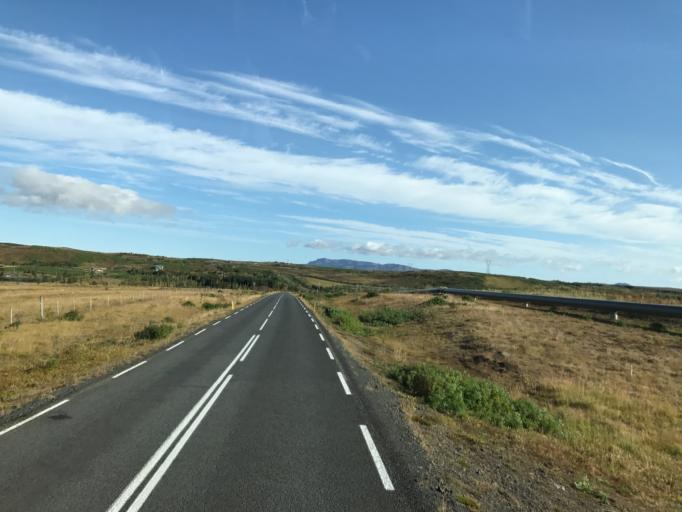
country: IS
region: Capital Region
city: Mosfellsbaer
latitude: 64.1096
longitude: -21.6524
